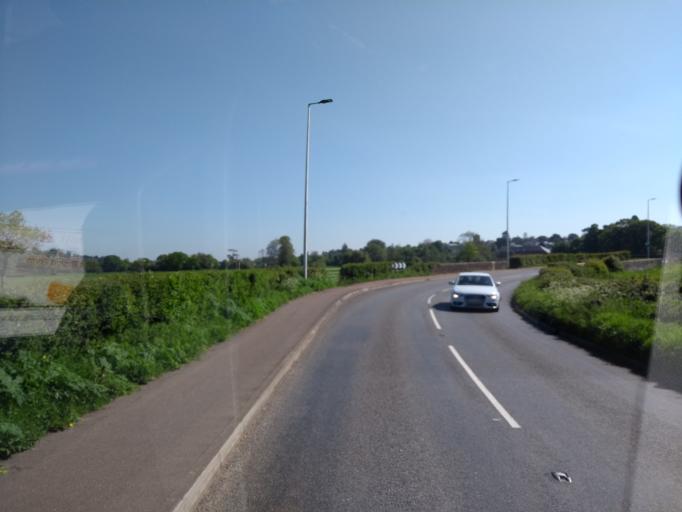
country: GB
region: England
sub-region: Devon
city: Axminster
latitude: 50.7791
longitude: -3.0099
